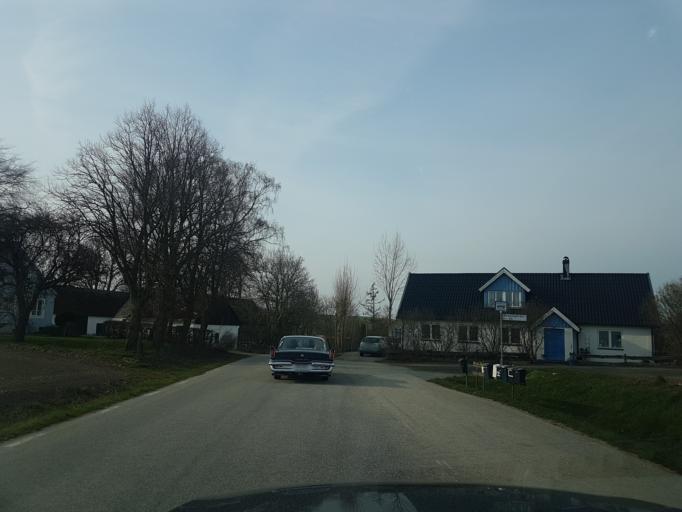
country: SE
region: Skane
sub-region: Ystads Kommun
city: Ystad
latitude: 55.4631
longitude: 13.8235
